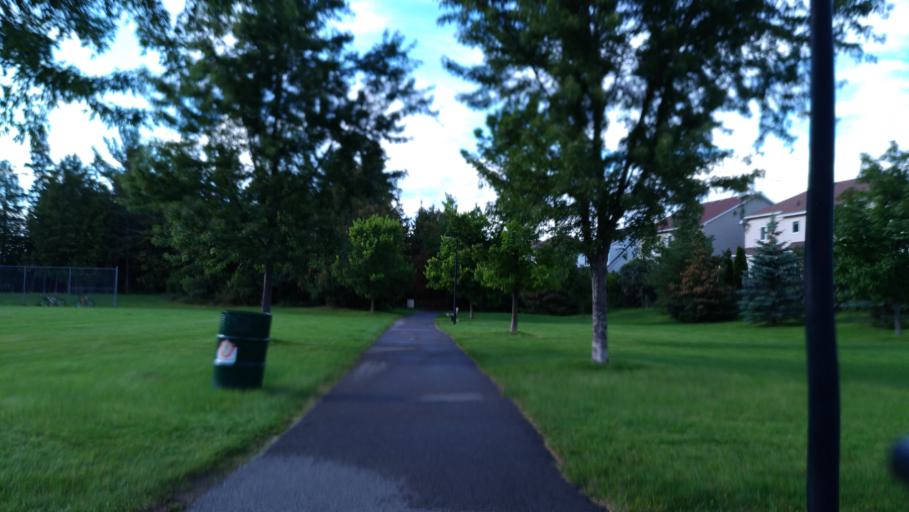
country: CA
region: Ontario
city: Bells Corners
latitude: 45.3511
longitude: -75.9404
